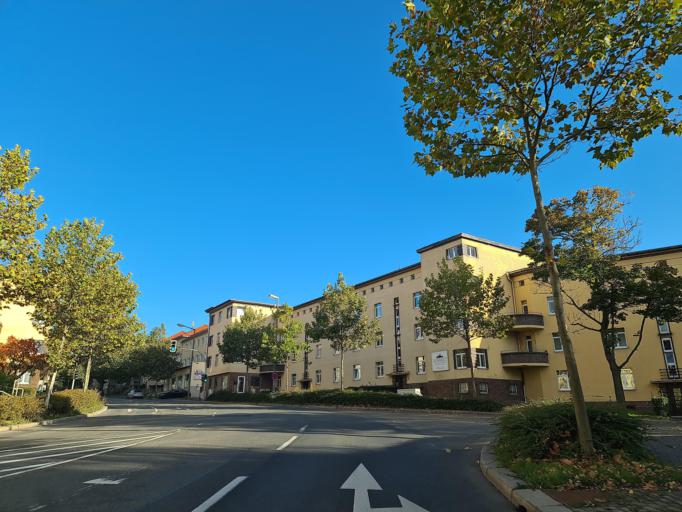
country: DE
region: Thuringia
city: Gera
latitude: 50.8842
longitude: 12.0951
